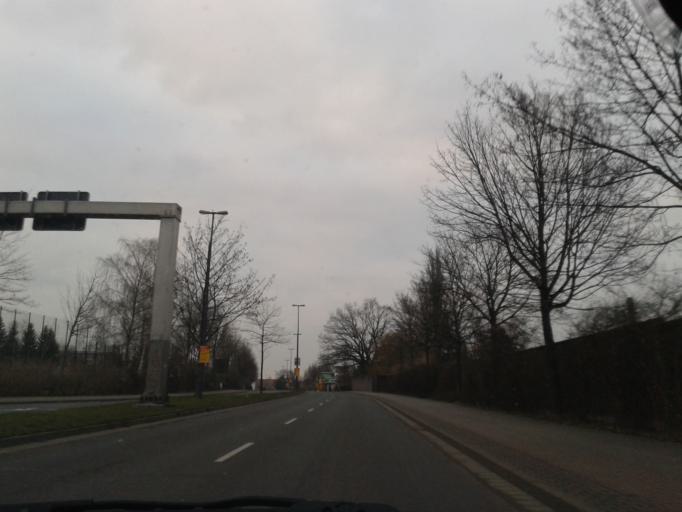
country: DE
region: Saxony
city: Dresden
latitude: 51.0101
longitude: 13.7834
